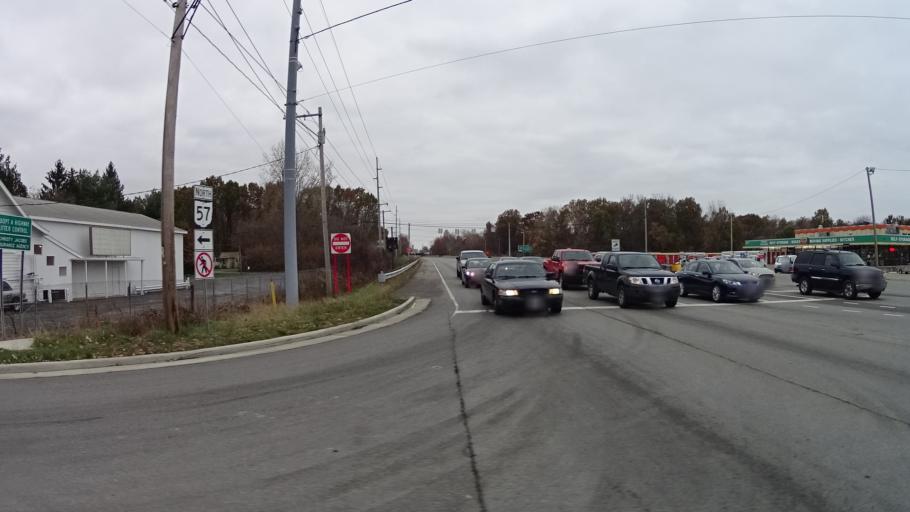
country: US
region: Ohio
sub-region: Lorain County
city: Sheffield
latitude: 41.4188
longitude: -82.1190
